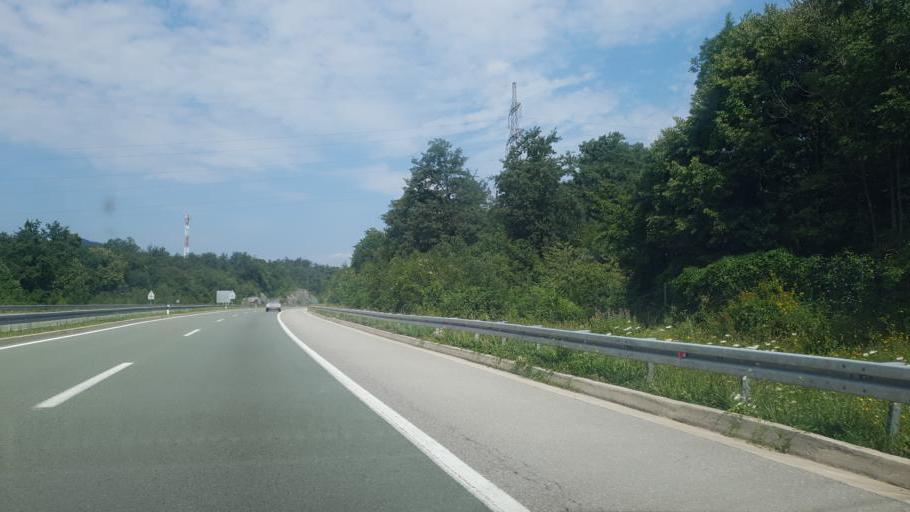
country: HR
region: Primorsko-Goranska
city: Matulji
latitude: 45.3815
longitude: 14.3065
